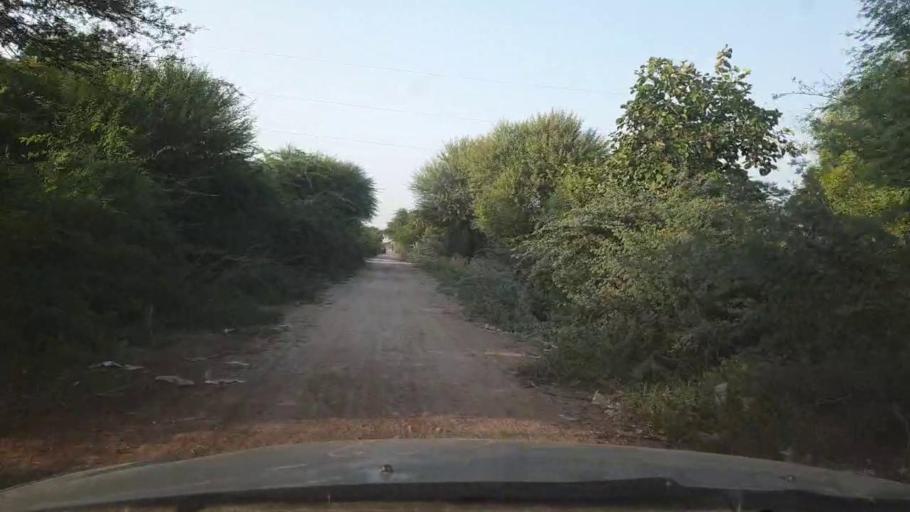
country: PK
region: Sindh
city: Tando Ghulam Ali
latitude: 25.1603
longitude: 68.9747
